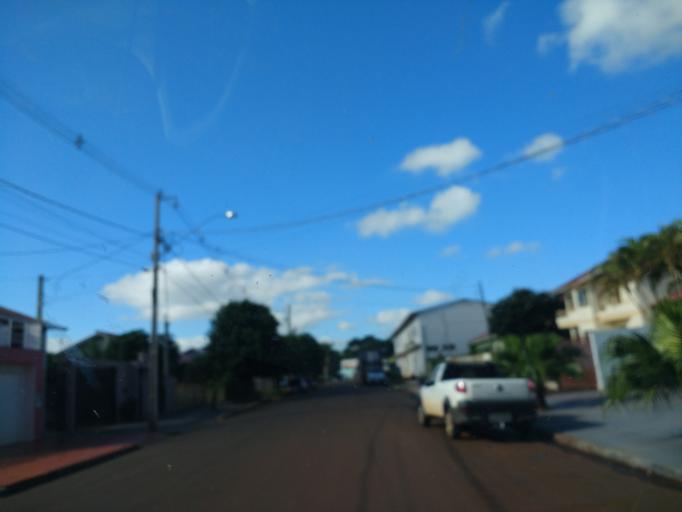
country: BR
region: Parana
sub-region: Palotina
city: Palotina
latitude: -24.4117
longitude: -53.5245
